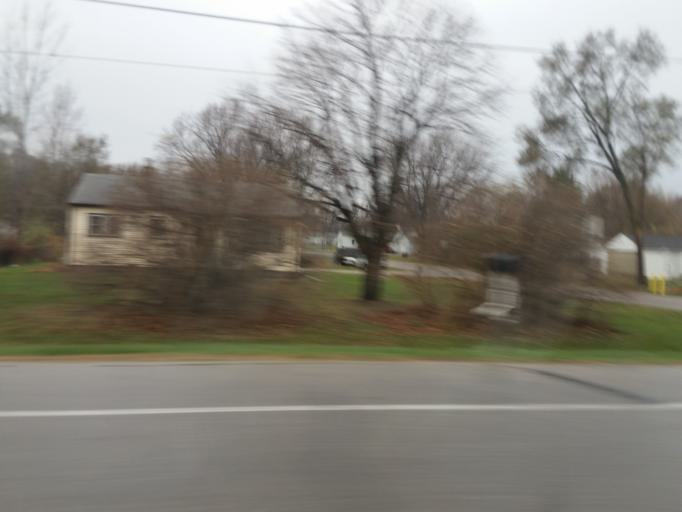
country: US
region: Iowa
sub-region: Black Hawk County
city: Elk Run Heights
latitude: 42.4092
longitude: -92.2648
